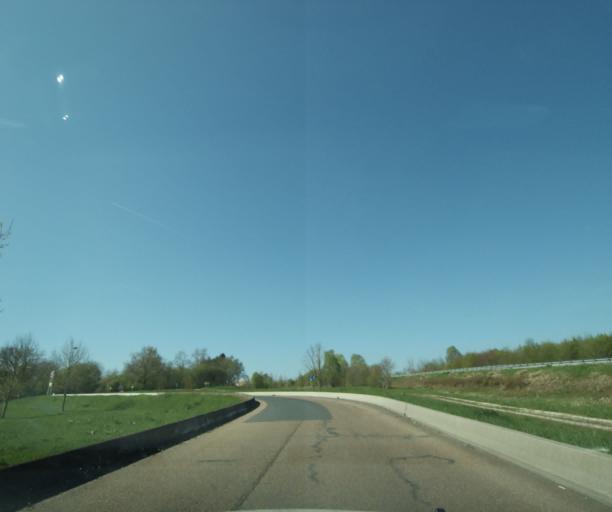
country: FR
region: Bourgogne
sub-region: Departement de la Nievre
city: Pouilly-sur-Loire
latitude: 47.3391
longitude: 2.9289
